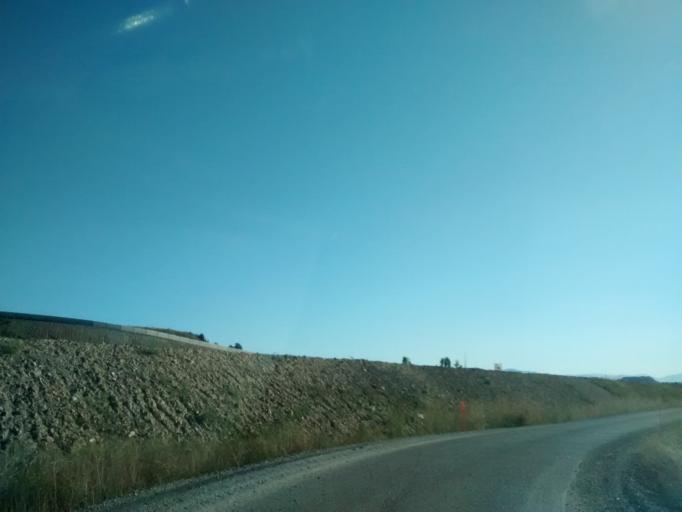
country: ES
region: Aragon
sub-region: Provincia de Huesca
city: Bailo
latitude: 42.5621
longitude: -0.7864
